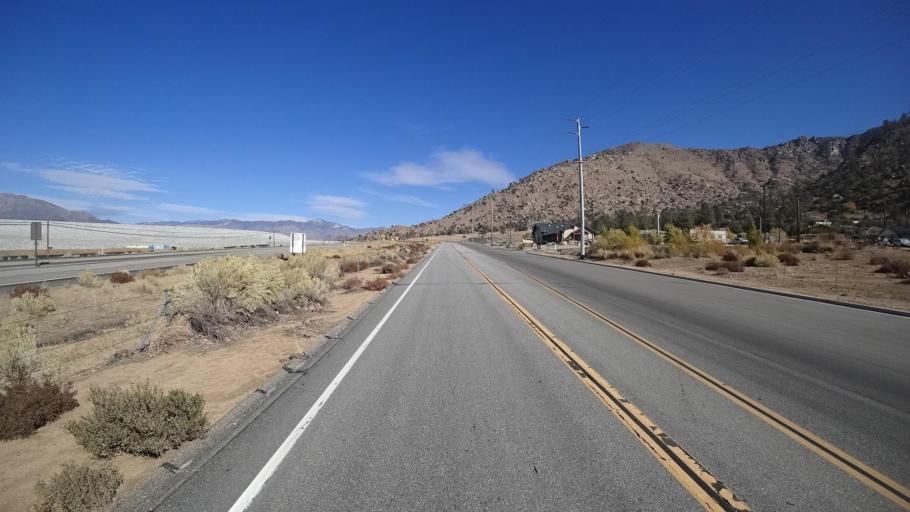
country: US
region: California
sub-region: Kern County
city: Lake Isabella
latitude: 35.6387
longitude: -118.4644
